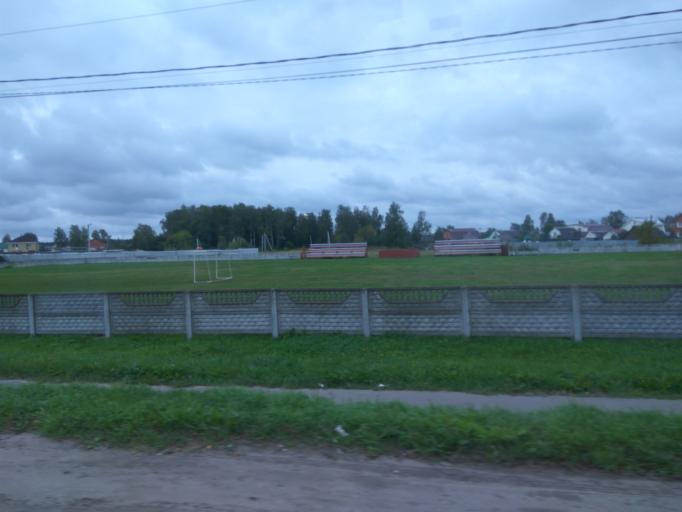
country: RU
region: Moskovskaya
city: Malyshevo
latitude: 55.4989
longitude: 38.3541
